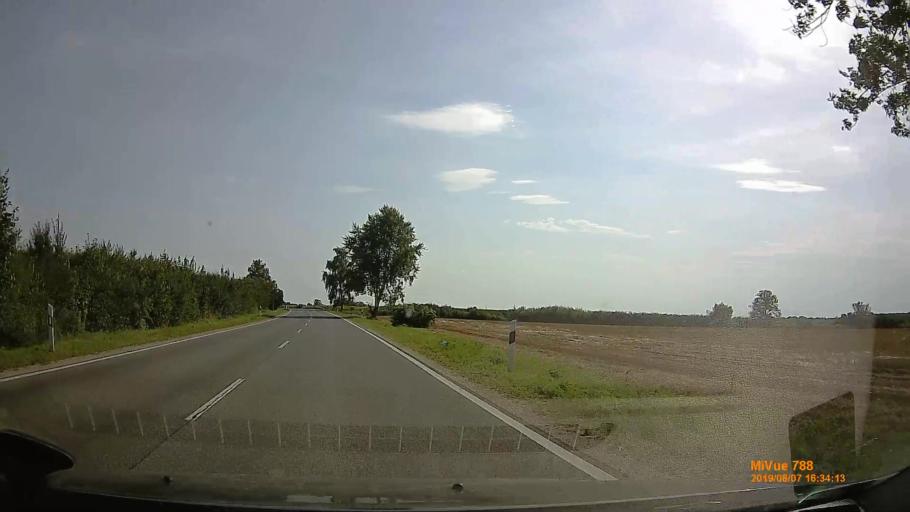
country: SI
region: Lendava-Lendva
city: Lendava
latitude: 46.6243
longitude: 16.4669
